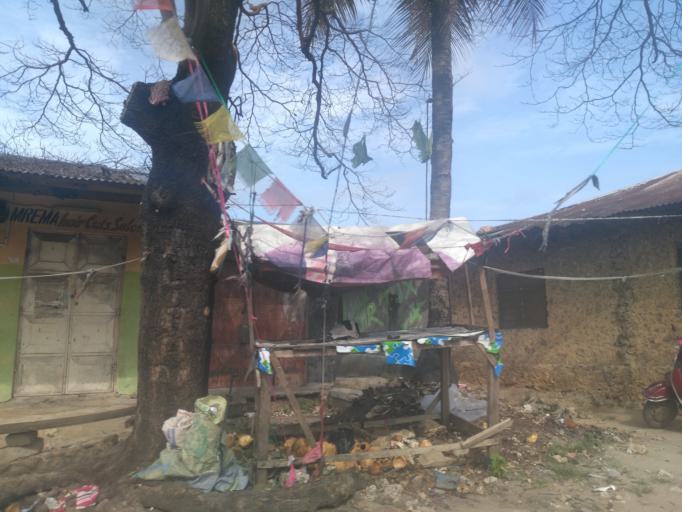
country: TZ
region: Zanzibar Urban/West
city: Zanzibar
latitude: -6.1664
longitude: 39.2105
